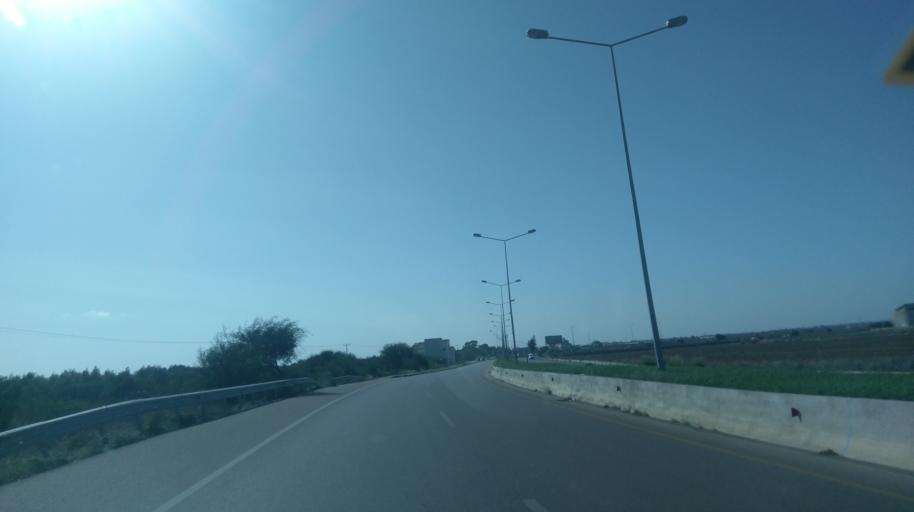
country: CY
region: Ammochostos
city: Trikomo
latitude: 35.2325
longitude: 33.8989
